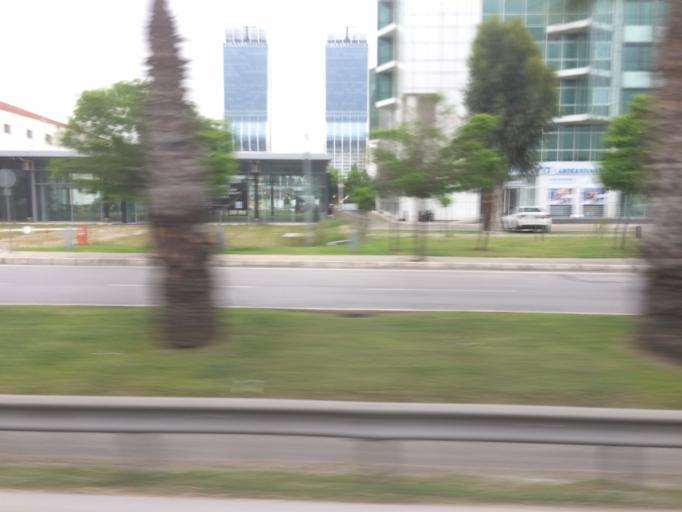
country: TR
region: Izmir
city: Izmir
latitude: 38.4507
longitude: 27.1701
